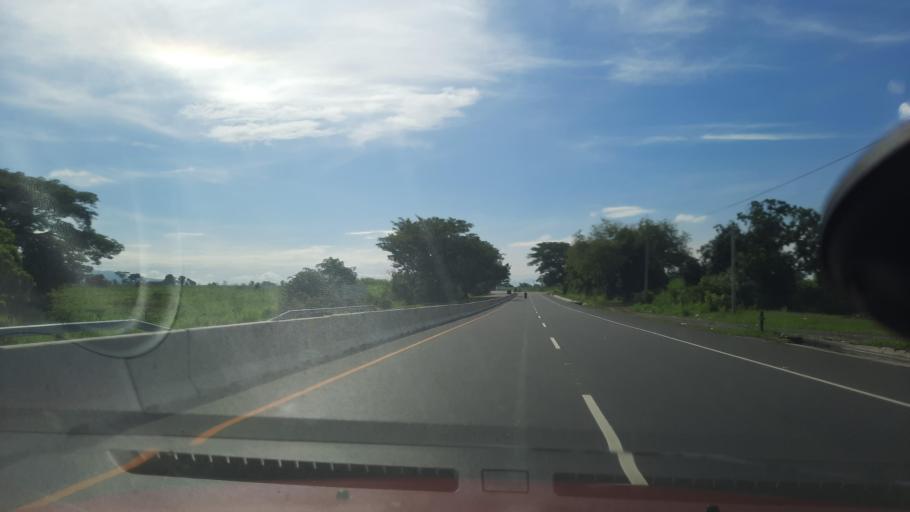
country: SV
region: La Paz
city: El Rosario
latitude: 13.4858
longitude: -88.9883
